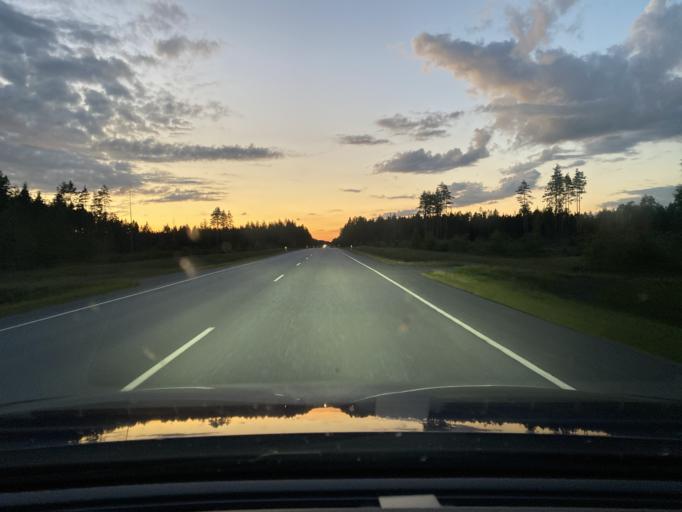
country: FI
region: Varsinais-Suomi
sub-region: Loimaa
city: Oripaeae
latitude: 60.9110
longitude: 22.6932
